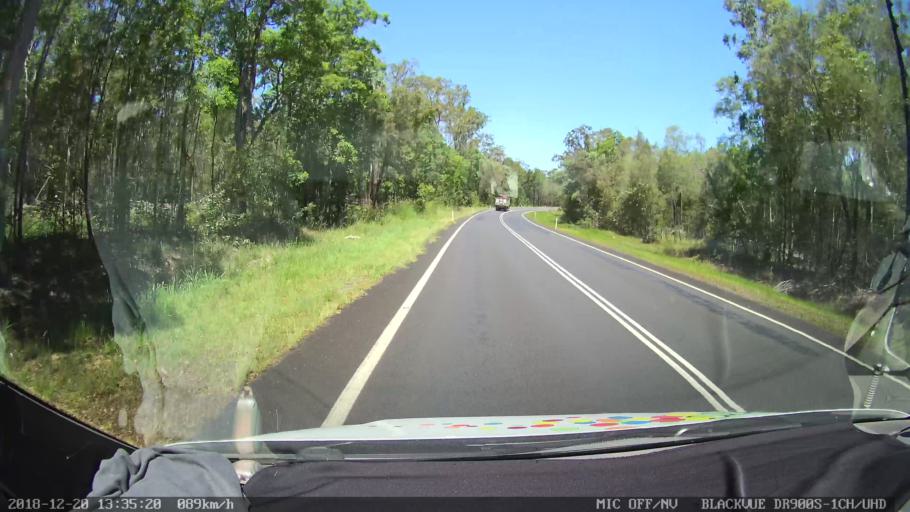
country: AU
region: New South Wales
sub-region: Clarence Valley
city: Gordon
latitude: -29.2683
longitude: 152.9906
